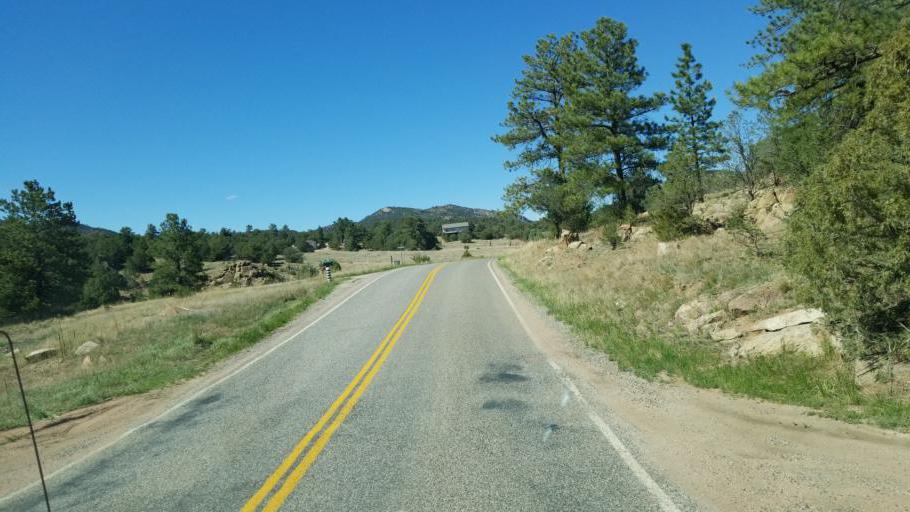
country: US
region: Colorado
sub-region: Custer County
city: Westcliffe
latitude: 38.3665
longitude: -105.4621
